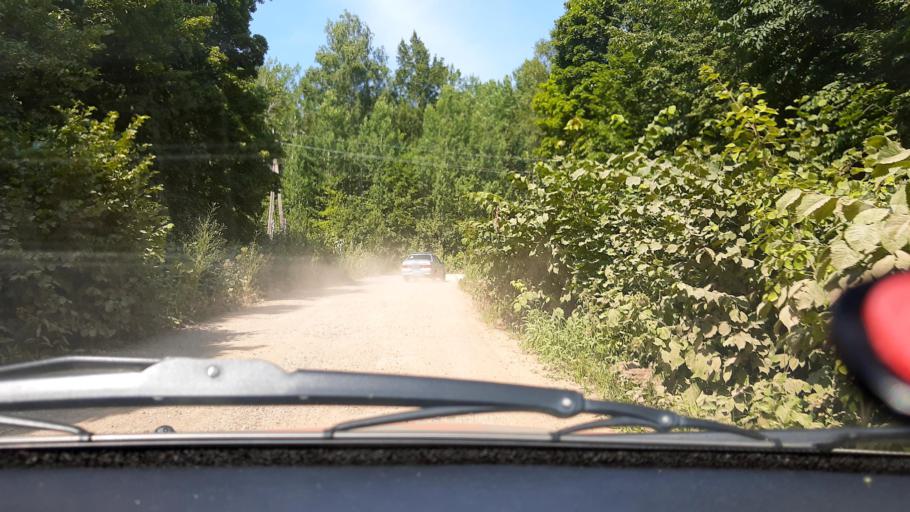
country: RU
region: Bashkortostan
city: Karmaskaly
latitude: 54.3892
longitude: 55.8922
